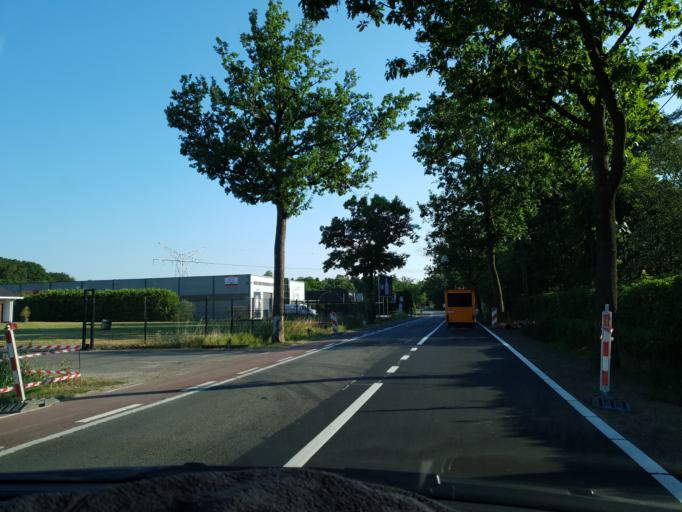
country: BE
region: Flanders
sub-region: Provincie Antwerpen
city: Oostmalle
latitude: 51.2847
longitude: 4.7240
